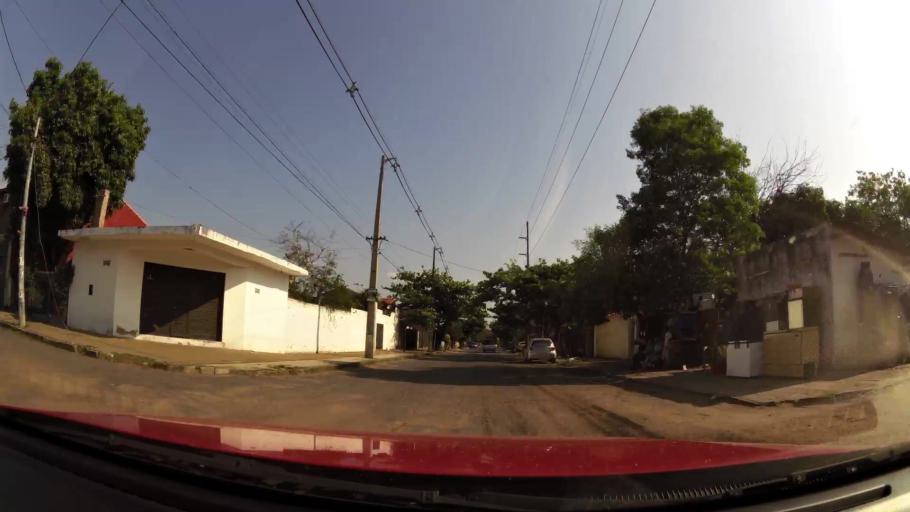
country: PY
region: Asuncion
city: Asuncion
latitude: -25.3157
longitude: -57.6340
